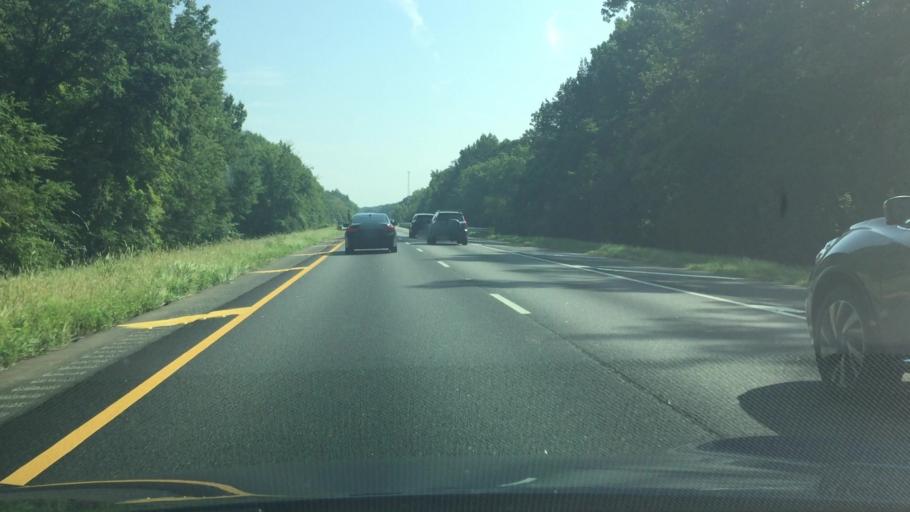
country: US
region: Alabama
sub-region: Montgomery County
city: Montgomery
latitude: 32.2231
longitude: -86.3932
